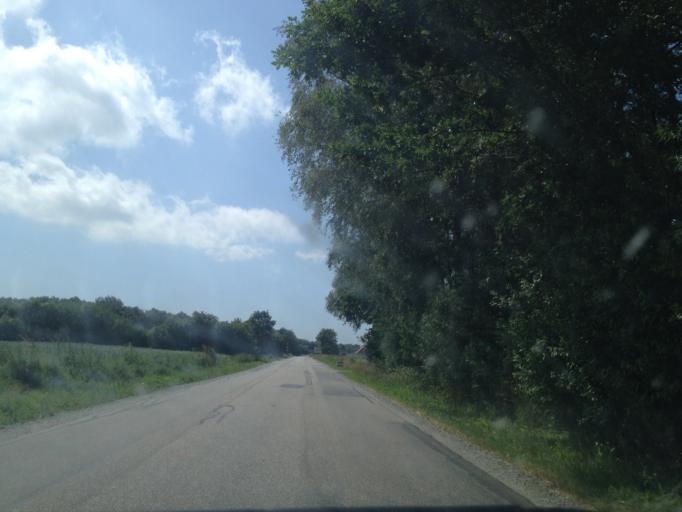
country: DK
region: South Denmark
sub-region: Kolding Kommune
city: Vamdrup
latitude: 55.3885
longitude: 9.2475
